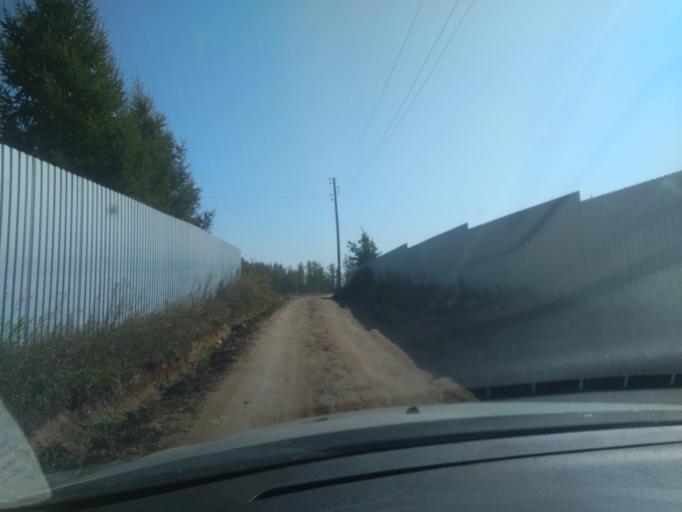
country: RU
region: Sverdlovsk
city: Pokrovskoye
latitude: 56.4363
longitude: 61.6010
